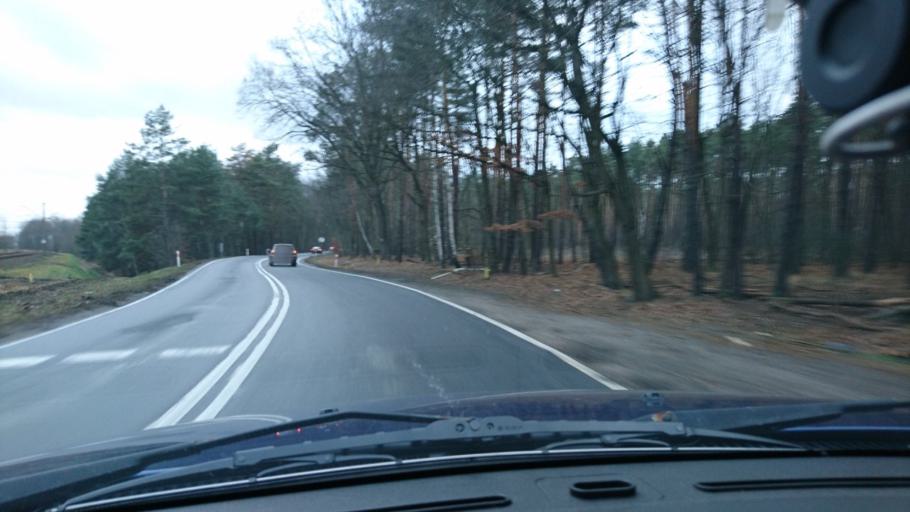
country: PL
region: Opole Voivodeship
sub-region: Powiat kluczborski
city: Kluczbork
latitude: 50.9584
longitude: 18.3058
